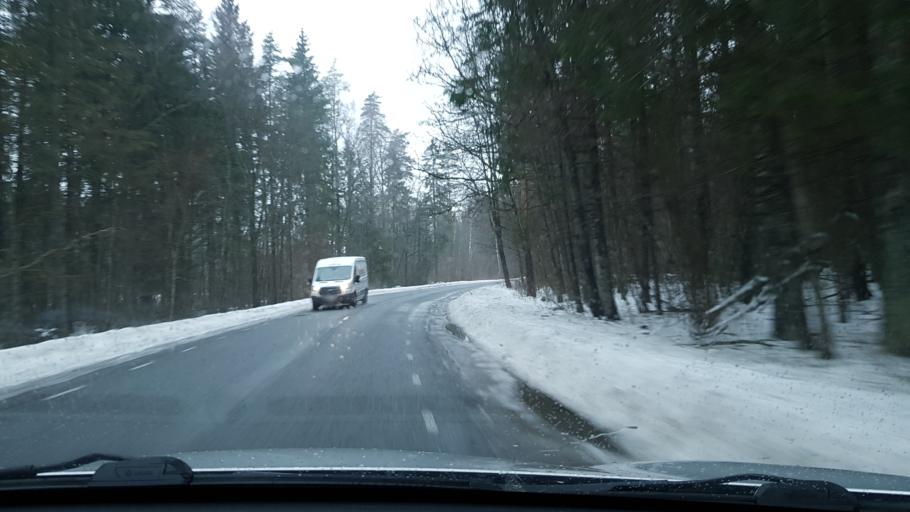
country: EE
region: Raplamaa
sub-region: Maerjamaa vald
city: Marjamaa
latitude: 58.8930
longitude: 24.4385
